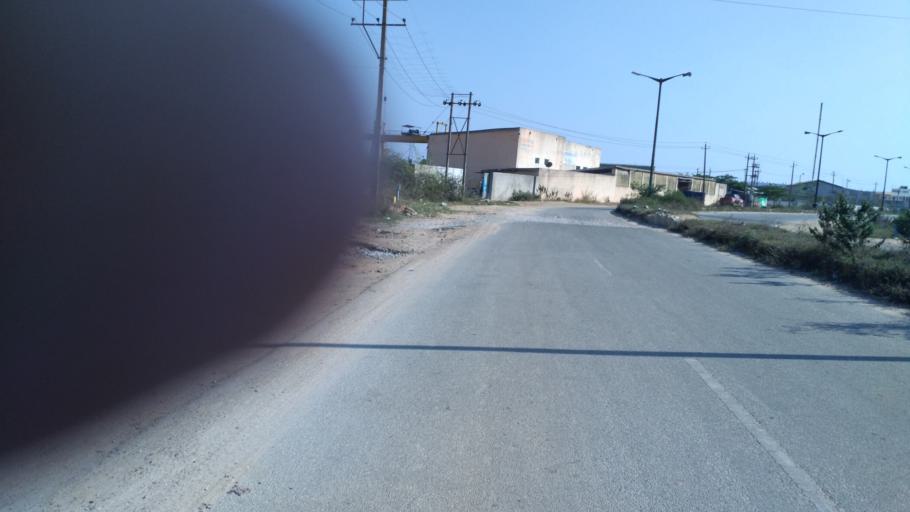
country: IN
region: Karnataka
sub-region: Hassan
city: Hassan
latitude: 12.9819
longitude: 76.1200
